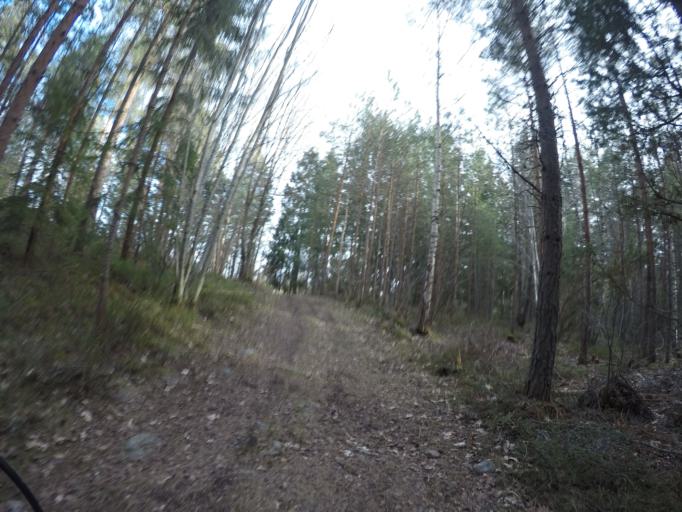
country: SE
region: Soedermanland
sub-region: Eskilstuna Kommun
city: Hallbybrunn
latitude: 59.4351
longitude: 16.4200
